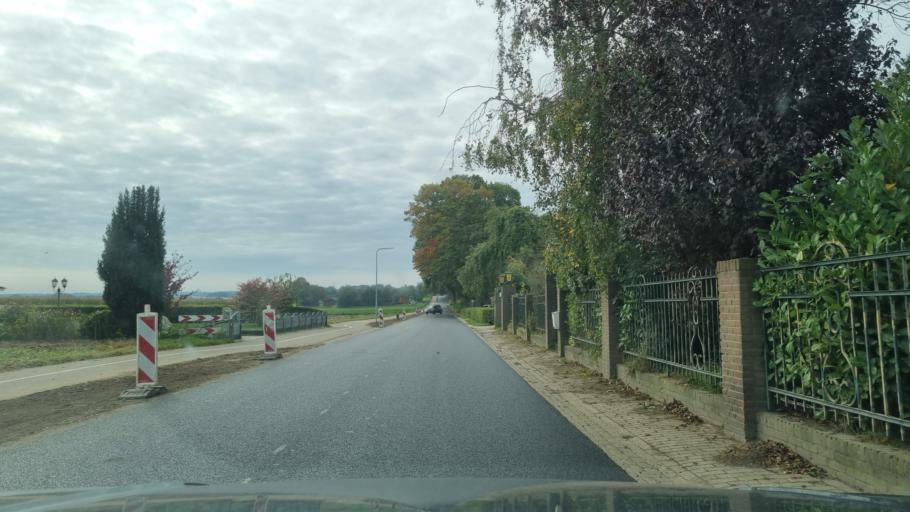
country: NL
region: Gelderland
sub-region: Gemeente Groesbeek
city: Groesbeek
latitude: 51.7963
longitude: 5.9514
